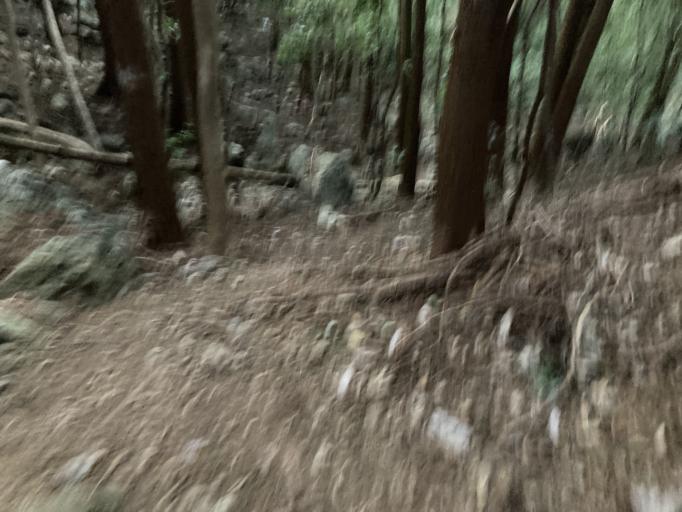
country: JP
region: Aichi
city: Tahara
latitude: 34.6082
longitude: 137.1468
